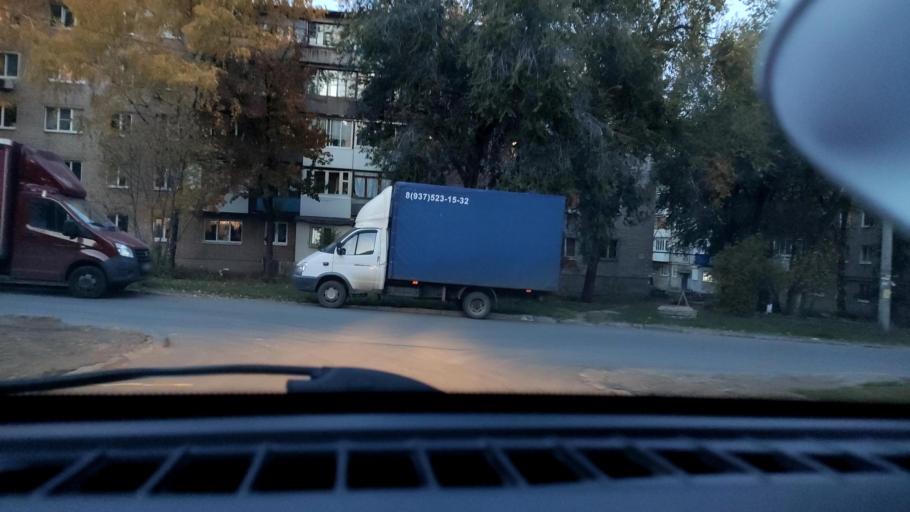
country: RU
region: Samara
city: Samara
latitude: 53.2195
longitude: 50.2250
